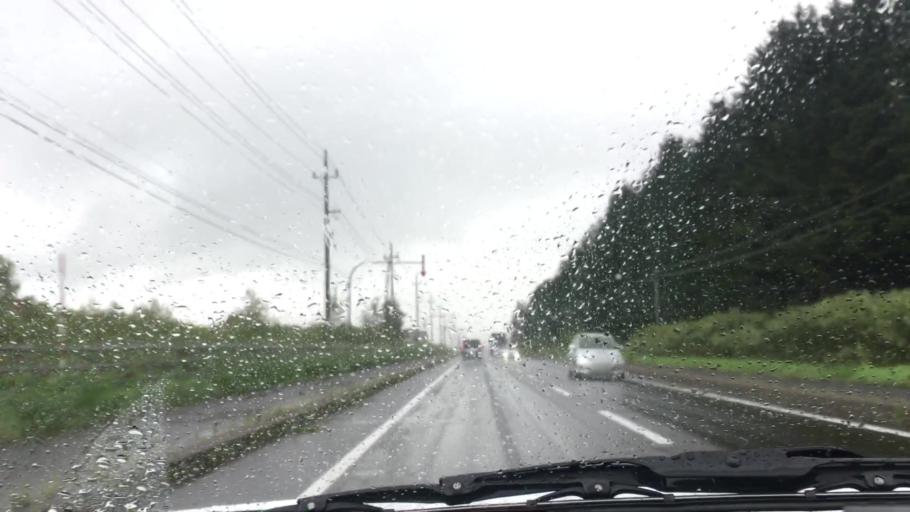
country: JP
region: Hokkaido
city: Niseko Town
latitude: 42.7433
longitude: 140.8905
